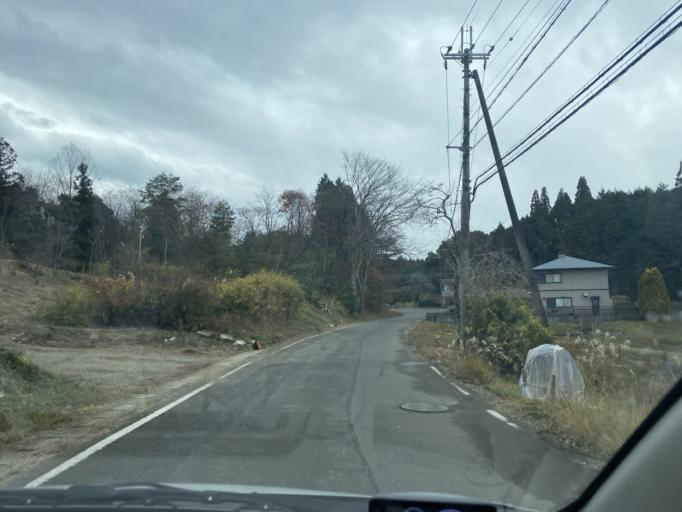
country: JP
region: Kyoto
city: Kameoka
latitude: 35.0554
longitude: 135.4525
